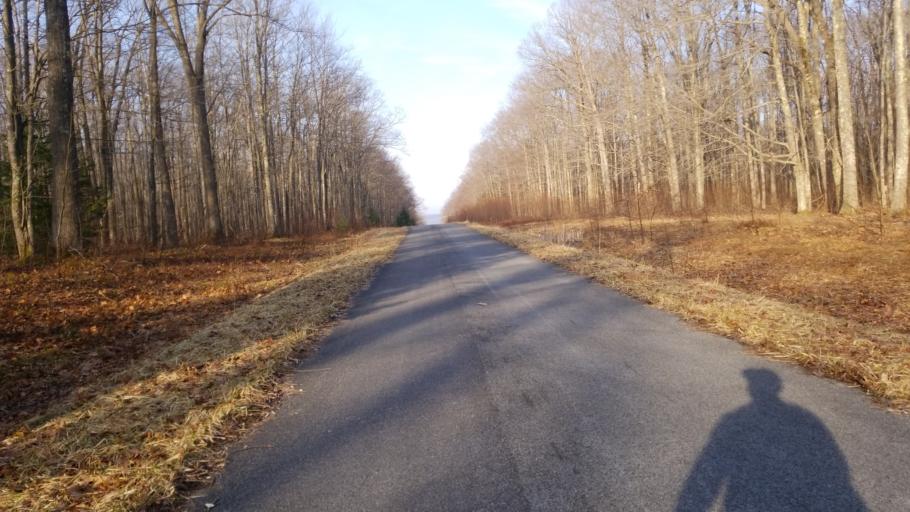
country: US
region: Pennsylvania
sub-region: Clearfield County
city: Shiloh
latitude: 41.2263
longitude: -78.2221
